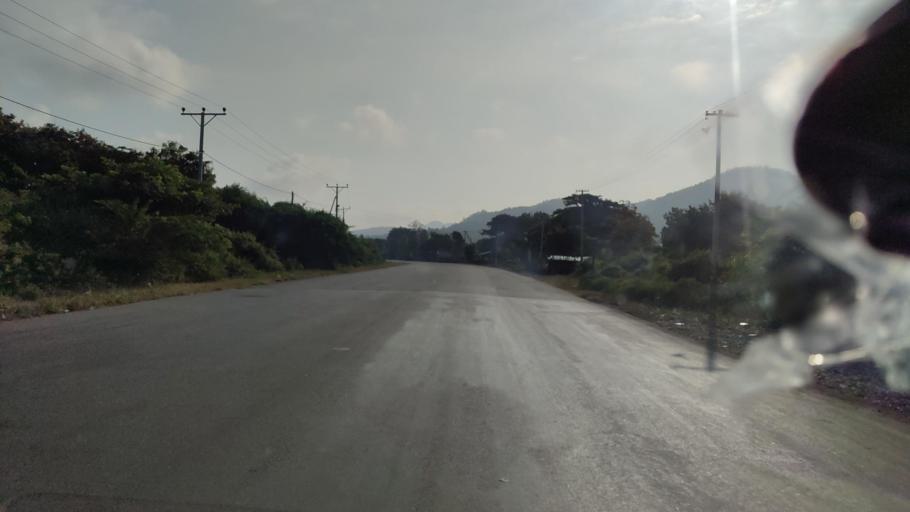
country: MM
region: Mandalay
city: Yamethin
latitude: 20.7517
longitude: 96.2650
